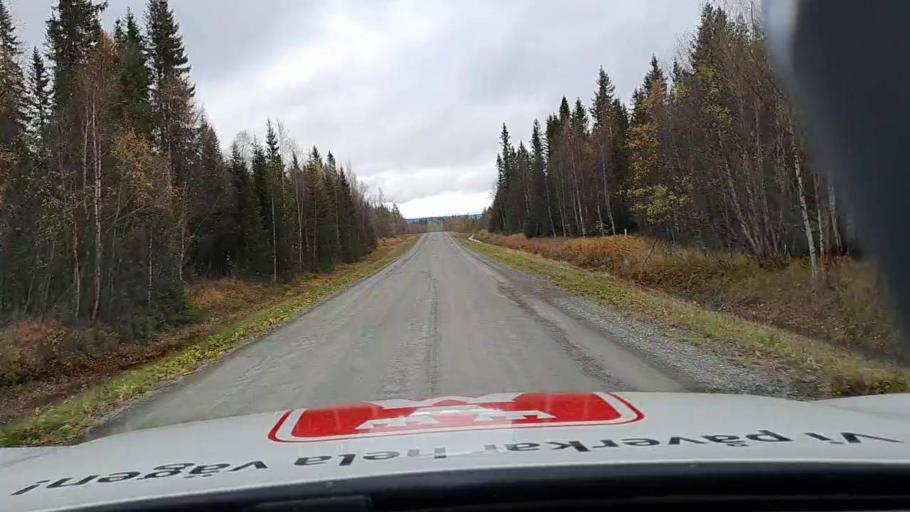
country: SE
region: Jaemtland
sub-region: Krokoms Kommun
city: Valla
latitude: 63.0477
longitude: 13.9603
